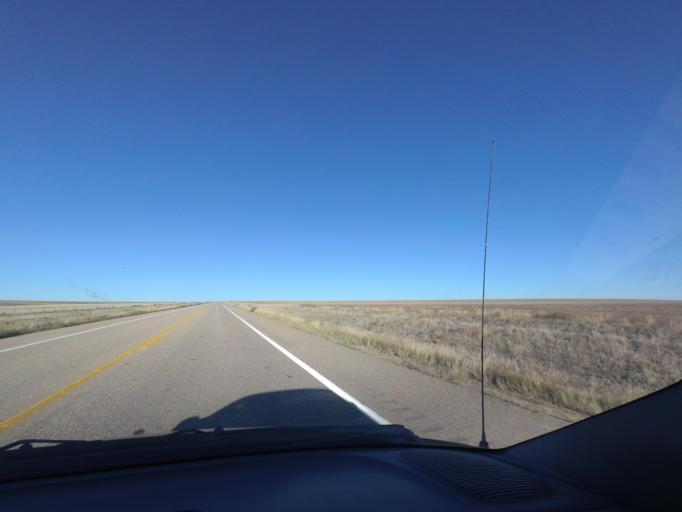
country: US
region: Colorado
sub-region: Arapahoe County
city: Byers
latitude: 39.7401
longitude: -103.7874
